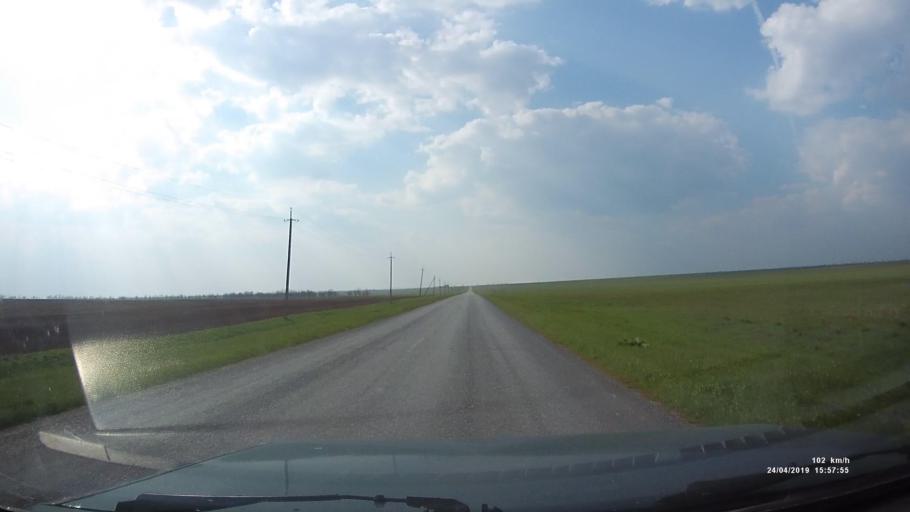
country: RU
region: Kalmykiya
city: Yashalta
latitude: 46.6095
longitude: 42.4996
